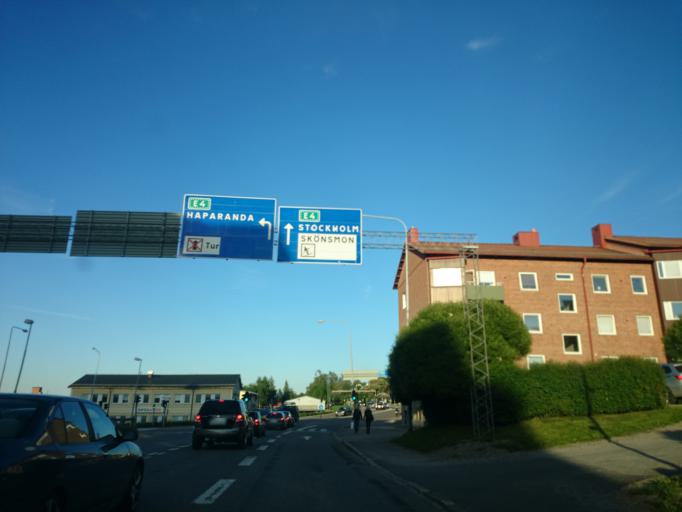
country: SE
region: Vaesternorrland
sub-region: Sundsvalls Kommun
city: Sundsvall
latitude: 62.3855
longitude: 17.3105
